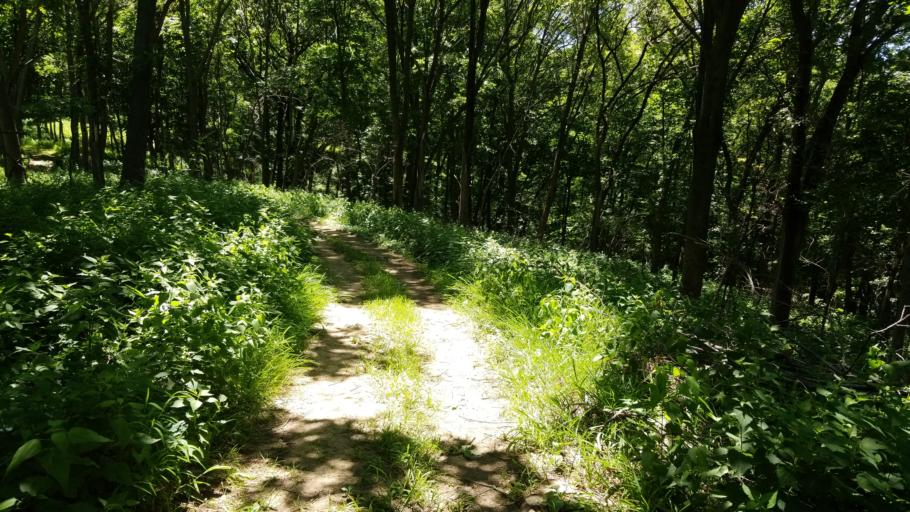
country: US
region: Iowa
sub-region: Pottawattamie County
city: Carter Lake
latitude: 41.3972
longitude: -95.9538
